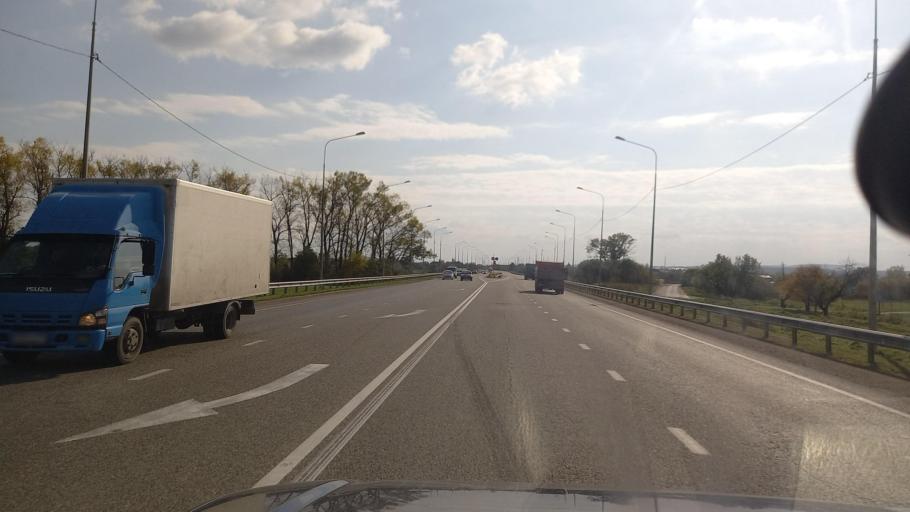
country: RU
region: Krasnodarskiy
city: Novoukrainskiy
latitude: 44.9017
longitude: 38.0359
